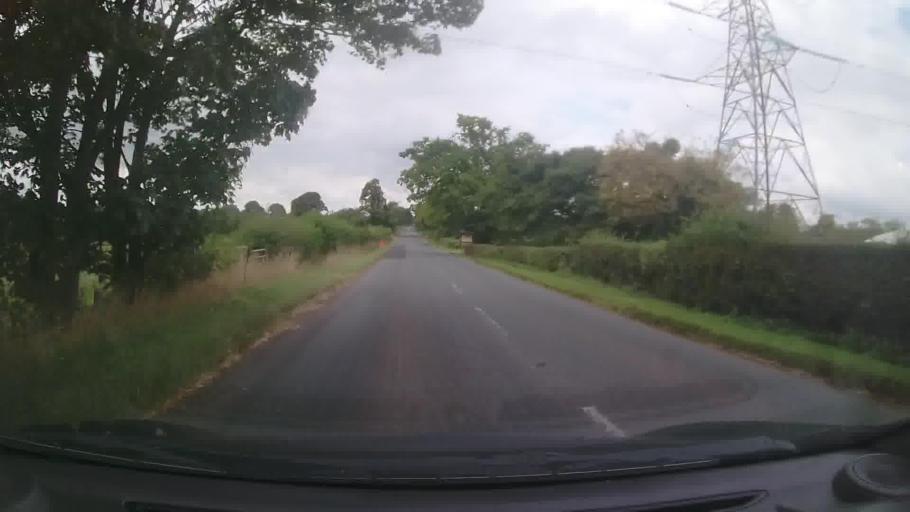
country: GB
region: England
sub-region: Shropshire
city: Whittington
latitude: 52.8863
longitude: -2.9632
